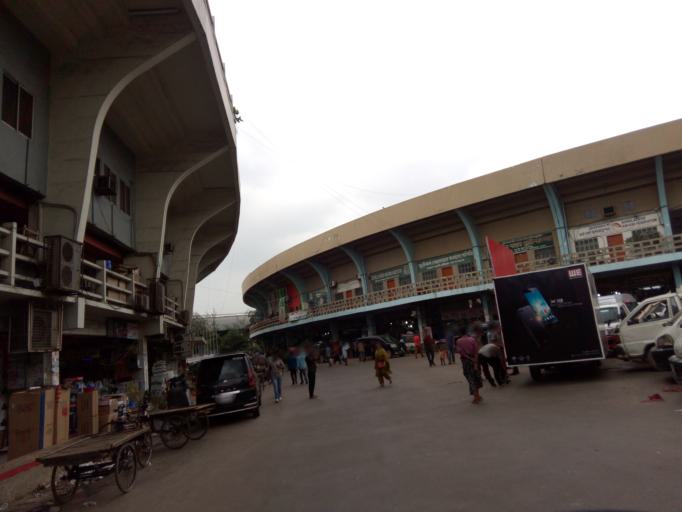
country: BD
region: Dhaka
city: Paltan
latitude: 23.7272
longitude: 90.4127
